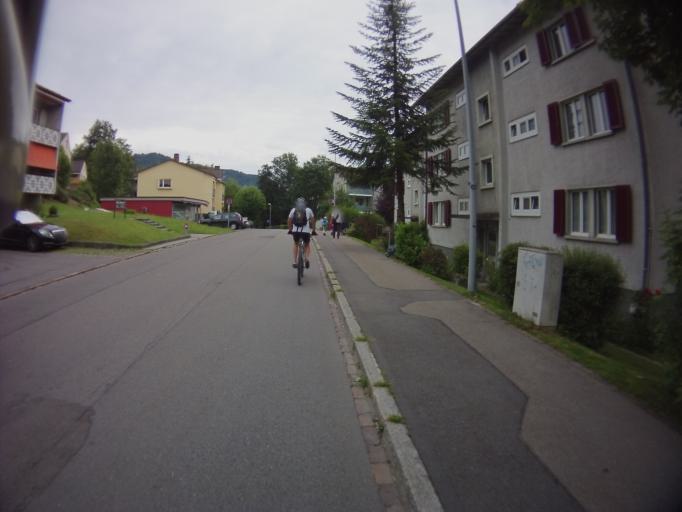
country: CH
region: Zurich
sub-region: Bezirk Horgen
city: Adliswil / Huendli-Zopf
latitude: 47.3171
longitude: 8.5175
